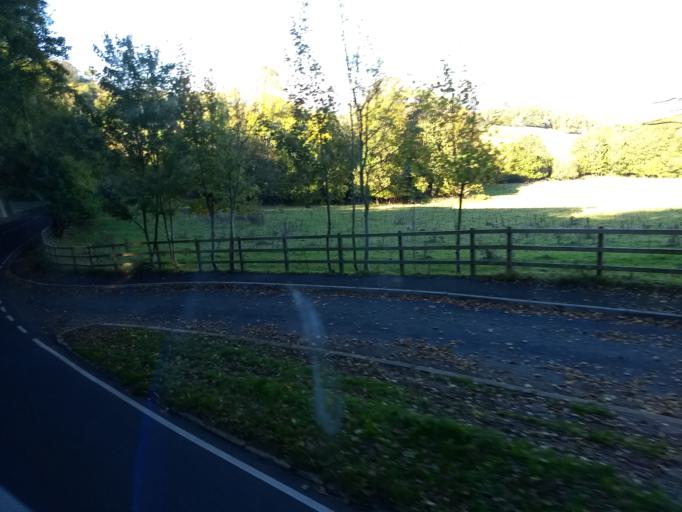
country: GB
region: England
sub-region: Isle of Wight
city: Shanklin
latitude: 50.6169
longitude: -1.1889
